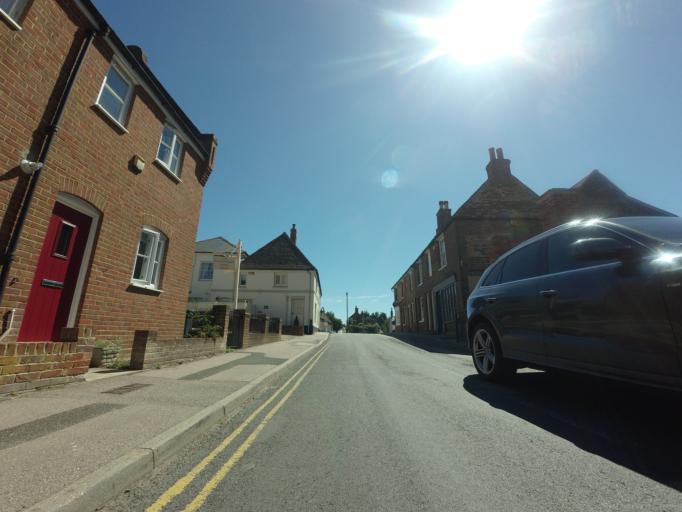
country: GB
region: England
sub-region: Kent
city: Ash
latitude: 51.2788
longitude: 1.2792
